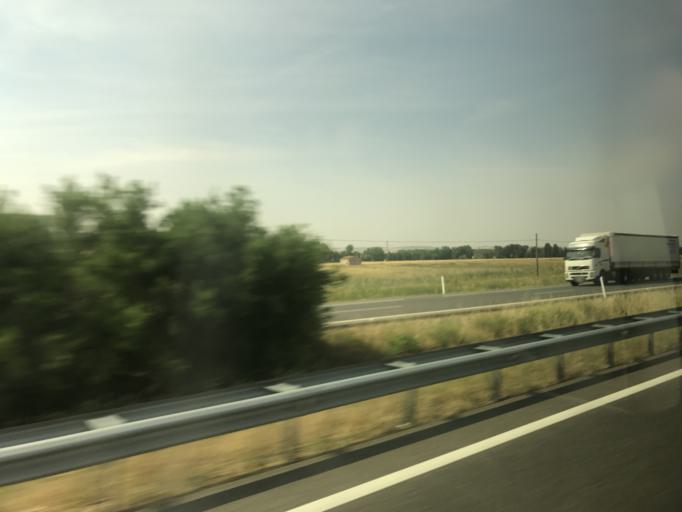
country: ES
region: Castille and Leon
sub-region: Provincia de Palencia
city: Palenzuela
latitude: 42.1280
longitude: -4.1329
